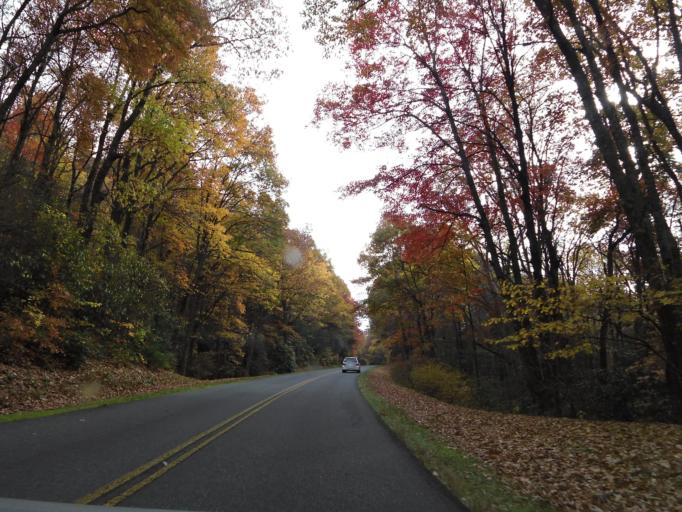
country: US
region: North Carolina
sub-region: Ashe County
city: Jefferson
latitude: 36.3087
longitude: -81.3615
